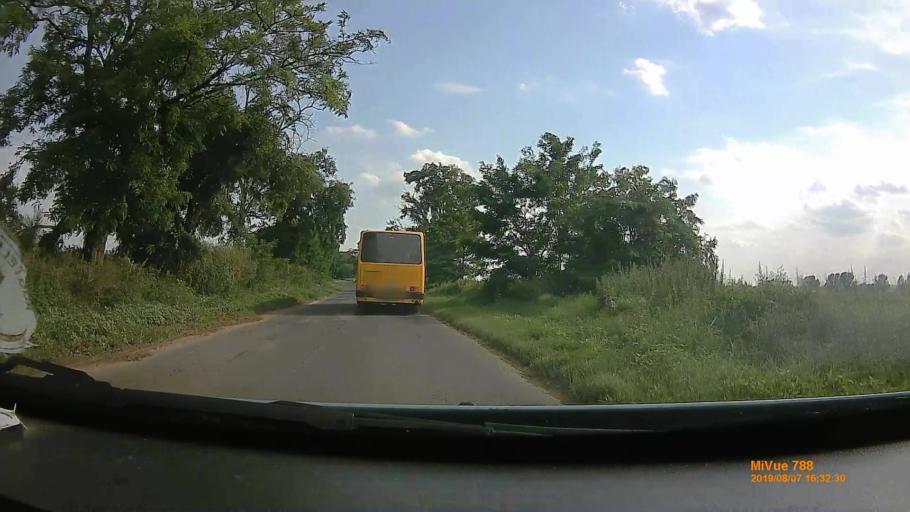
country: HU
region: Borsod-Abauj-Zemplen
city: Gonc
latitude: 48.4396
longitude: 21.2380
